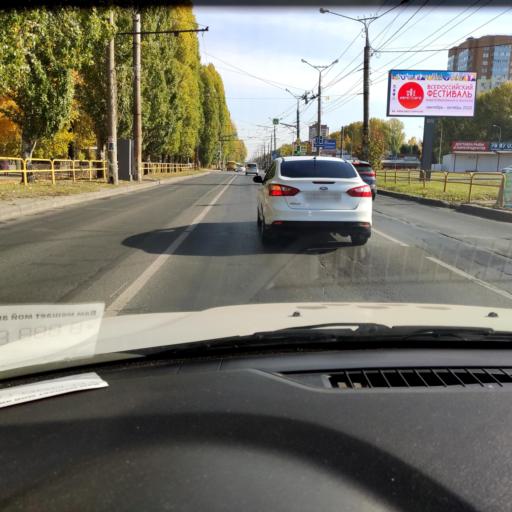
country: RU
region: Samara
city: Tol'yatti
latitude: 53.5088
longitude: 49.4211
